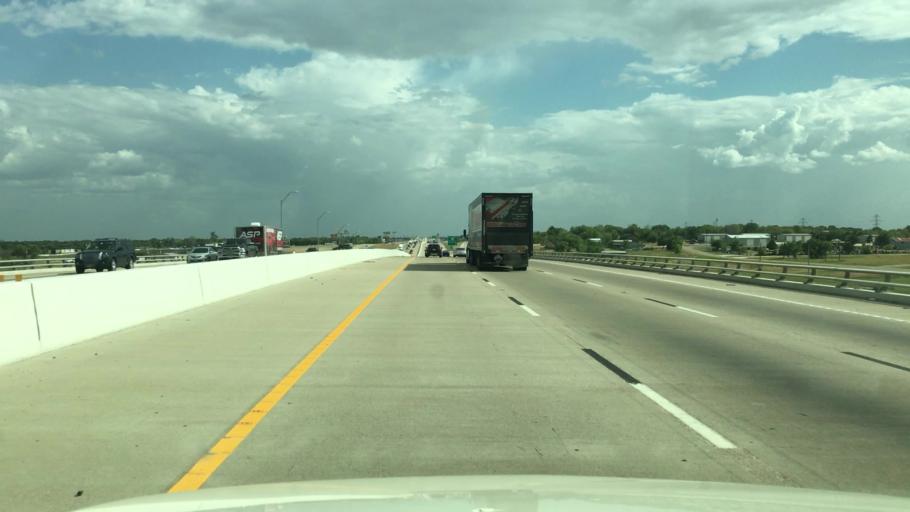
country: US
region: Texas
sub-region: McLennan County
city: Northcrest
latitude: 31.6883
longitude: -97.1000
